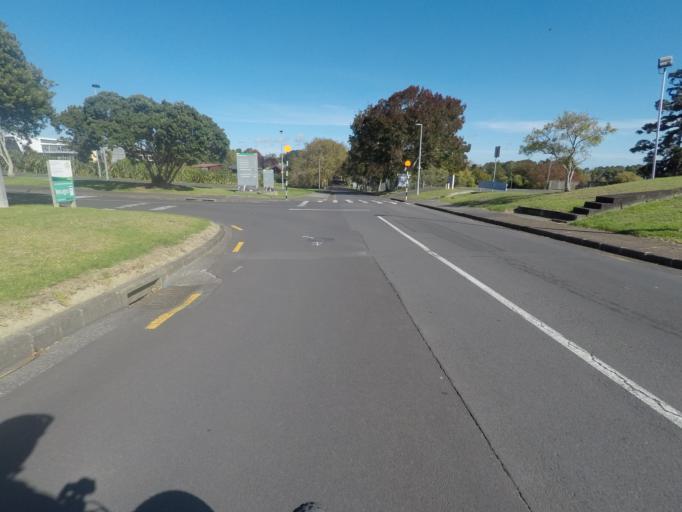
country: NZ
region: Auckland
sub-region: Auckland
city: Rosebank
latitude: -36.8782
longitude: 174.7097
